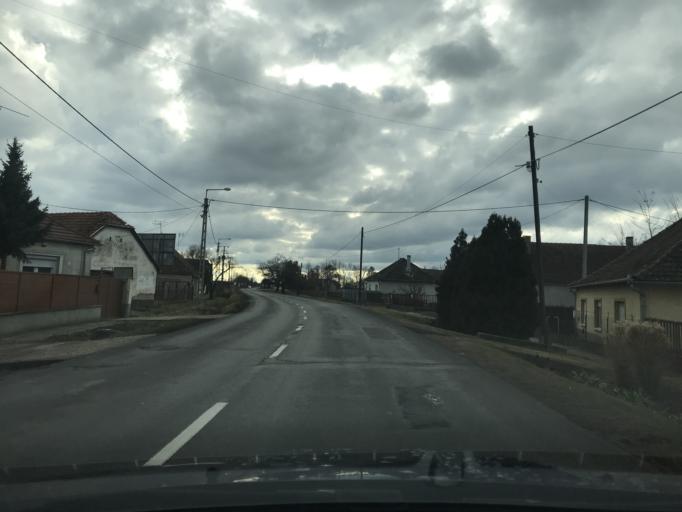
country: HU
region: Bacs-Kiskun
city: Csaszartoltes
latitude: 46.4146
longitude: 19.1720
